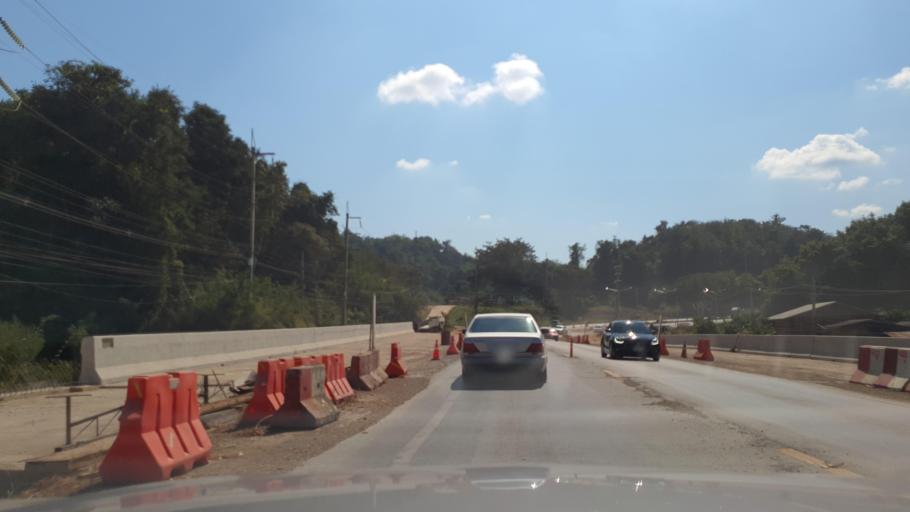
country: TH
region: Nan
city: Nan
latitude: 18.9204
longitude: 100.7657
